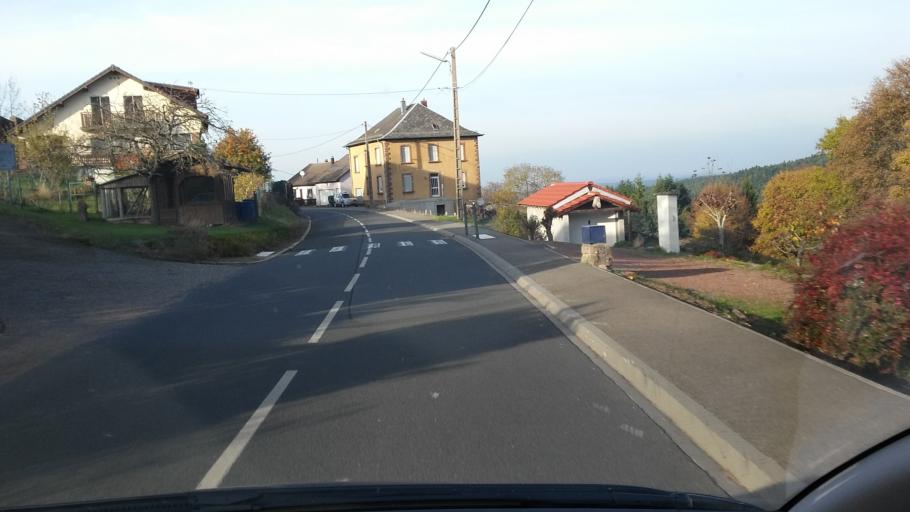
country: FR
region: Alsace
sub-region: Departement du Bas-Rhin
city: Wangenbourg-Engenthal
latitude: 48.6484
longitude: 7.2757
